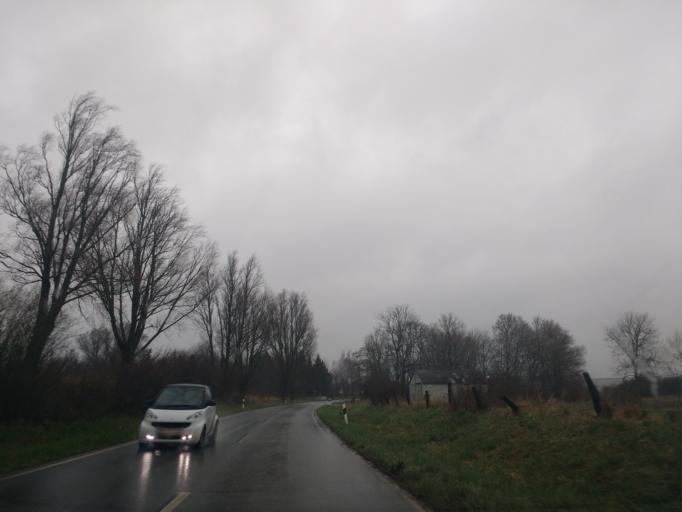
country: DE
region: Schleswig-Holstein
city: Blekendorf
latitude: 54.3062
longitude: 10.6520
